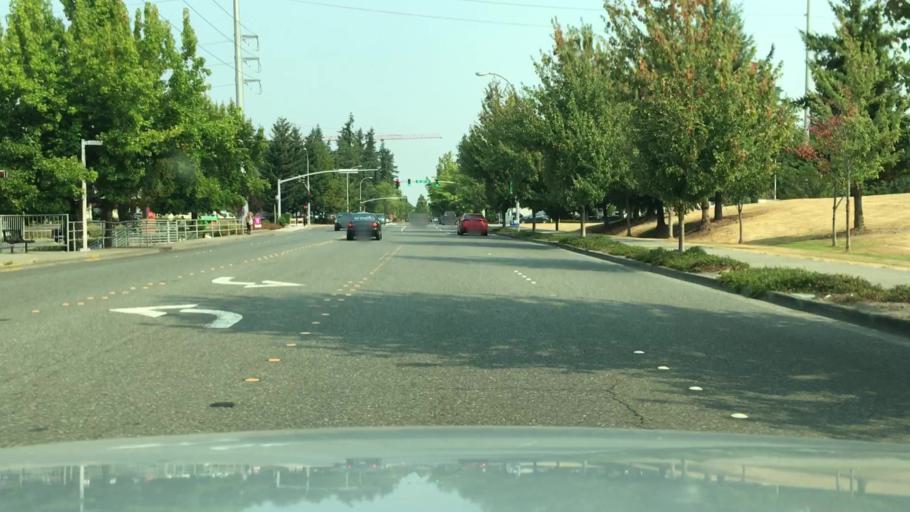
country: US
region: Washington
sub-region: King County
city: Redmond
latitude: 47.6305
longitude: -122.1323
